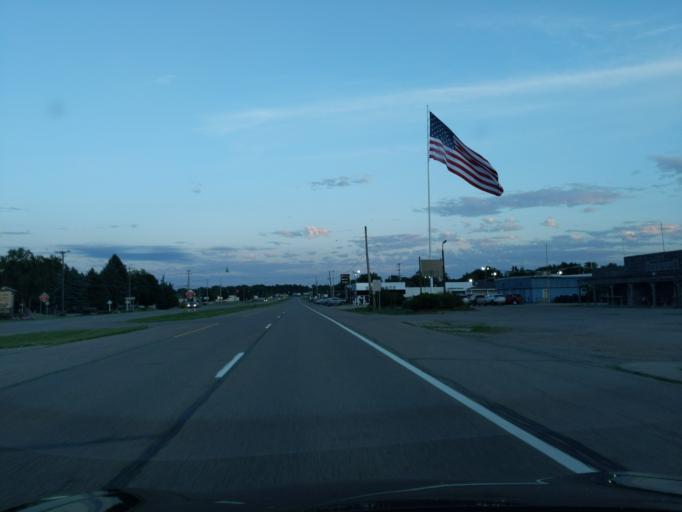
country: US
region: Michigan
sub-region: Clinton County
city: Saint Johns
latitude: 43.0158
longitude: -84.5602
